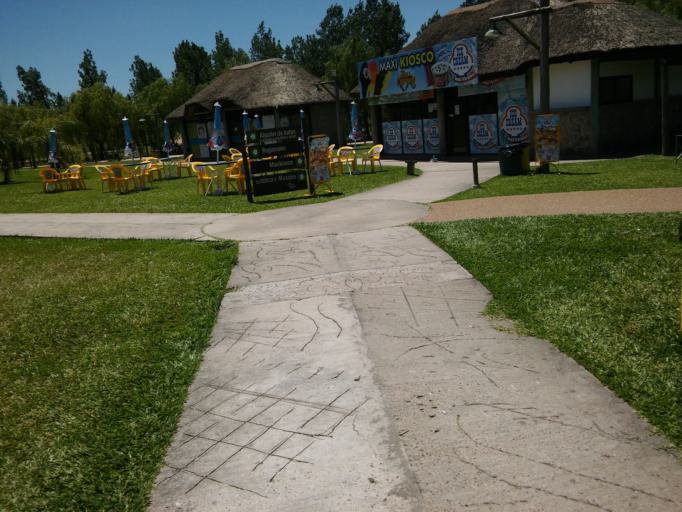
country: AR
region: Entre Rios
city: Concepcion del Uruguay
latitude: -32.4512
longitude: -58.2908
